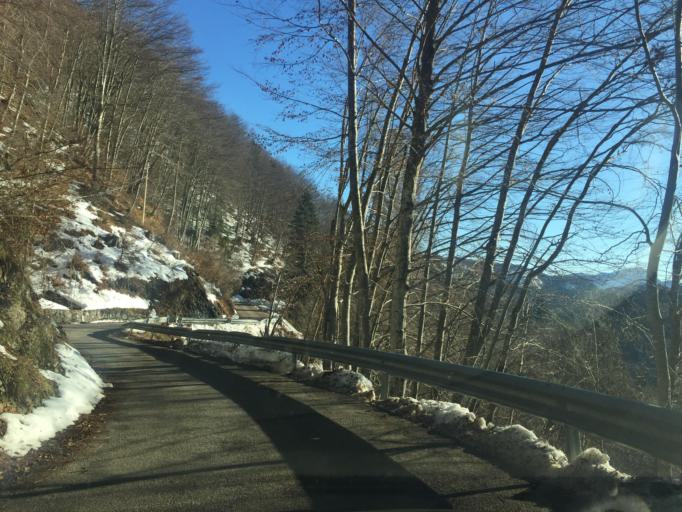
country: IT
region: Friuli Venezia Giulia
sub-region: Provincia di Udine
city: Lauco
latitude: 46.4442
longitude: 12.9374
